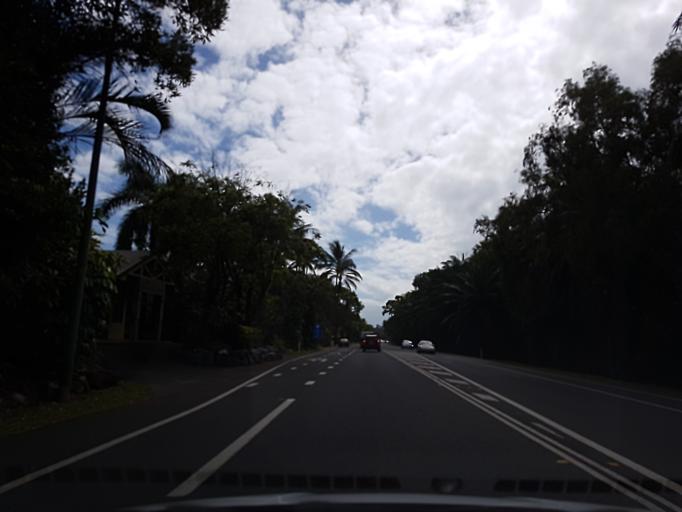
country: AU
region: Queensland
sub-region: Cairns
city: Port Douglas
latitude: -16.5005
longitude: 145.4633
